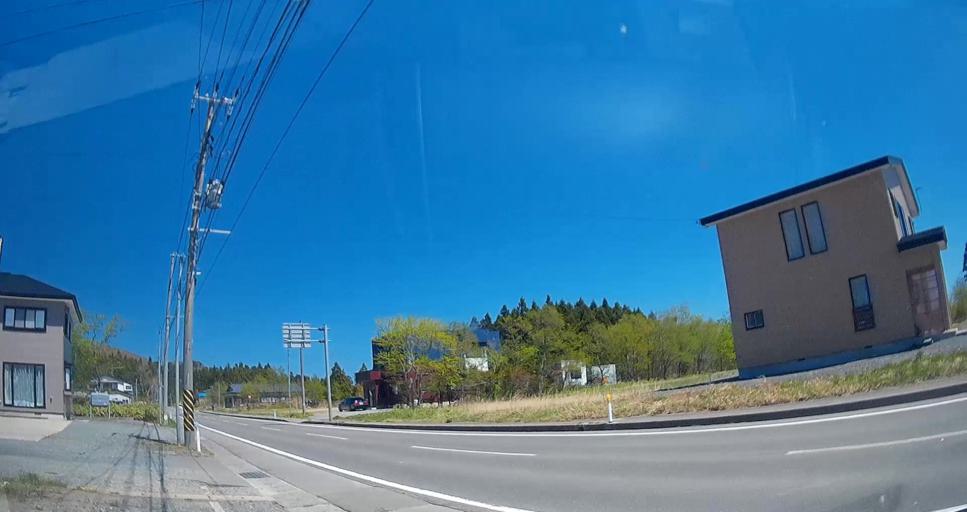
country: JP
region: Aomori
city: Mutsu
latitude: 41.0832
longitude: 141.3859
